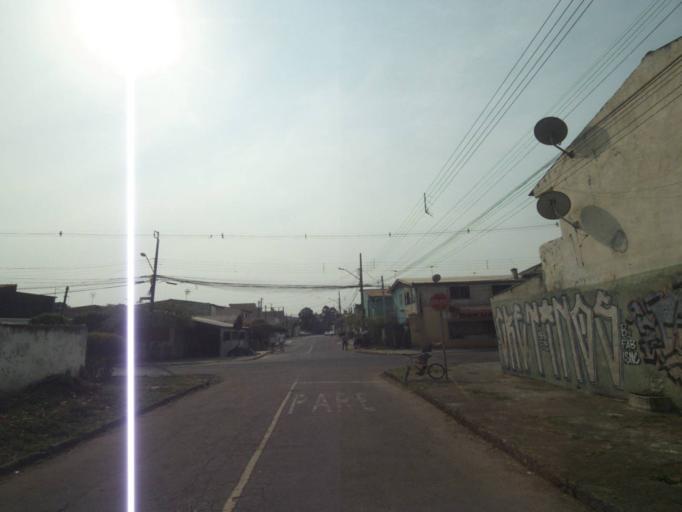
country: BR
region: Parana
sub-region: Sao Jose Dos Pinhais
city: Sao Jose dos Pinhais
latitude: -25.5251
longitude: -49.2727
